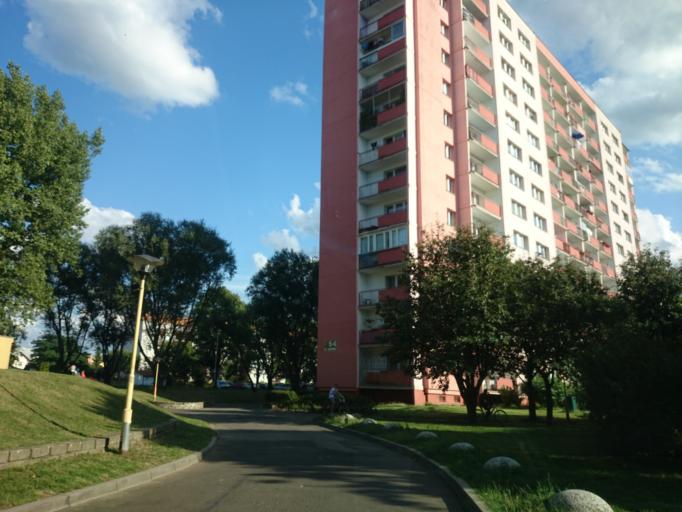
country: PL
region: West Pomeranian Voivodeship
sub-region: Szczecin
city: Szczecin
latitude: 53.3761
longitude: 14.6606
